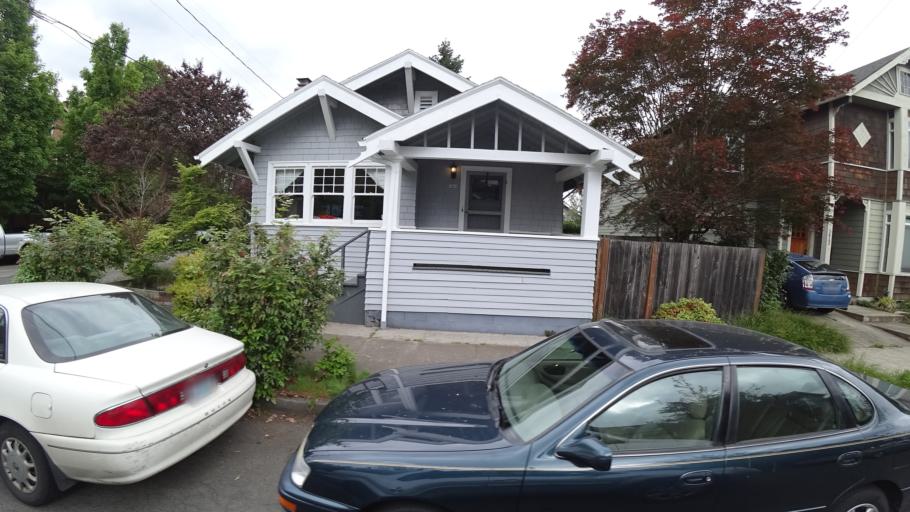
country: US
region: Oregon
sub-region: Multnomah County
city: Lents
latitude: 45.5127
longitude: -122.6171
